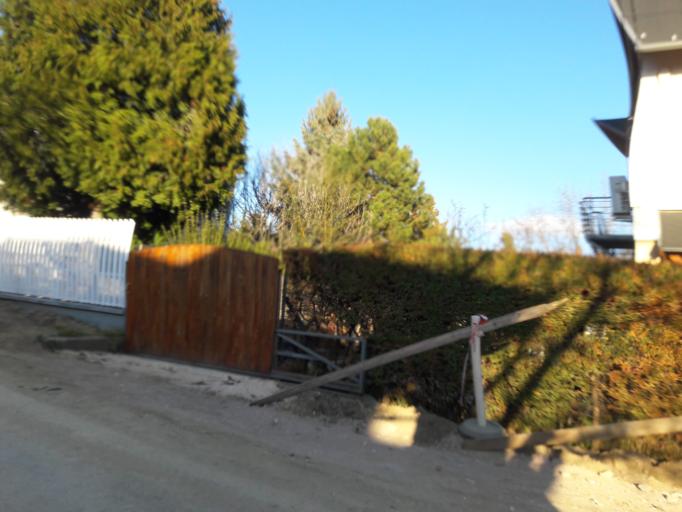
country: HU
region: Pest
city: Budaors
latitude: 47.4660
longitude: 18.9678
